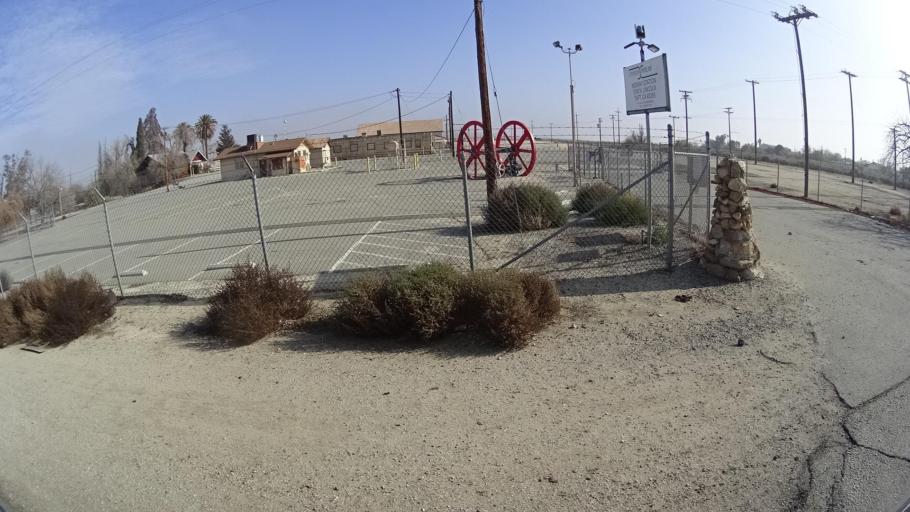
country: US
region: California
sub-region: Kern County
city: Ford City
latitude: 35.1662
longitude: -119.4653
